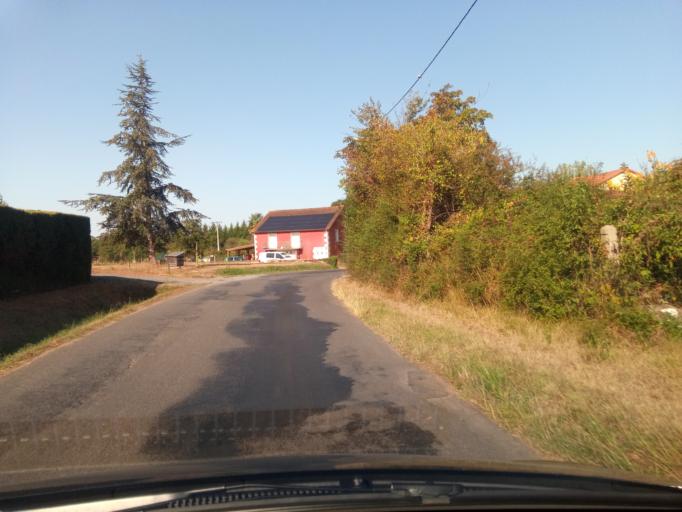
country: FR
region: Poitou-Charentes
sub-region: Departement de la Vienne
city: Saulge
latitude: 46.3299
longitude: 0.8357
